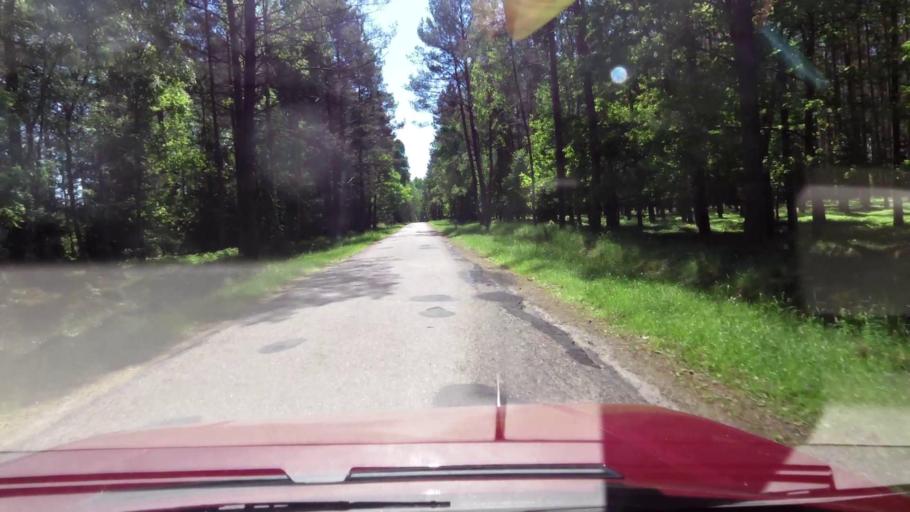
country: PL
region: West Pomeranian Voivodeship
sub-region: Powiat koszalinski
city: Bobolice
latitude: 54.0648
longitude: 16.5668
